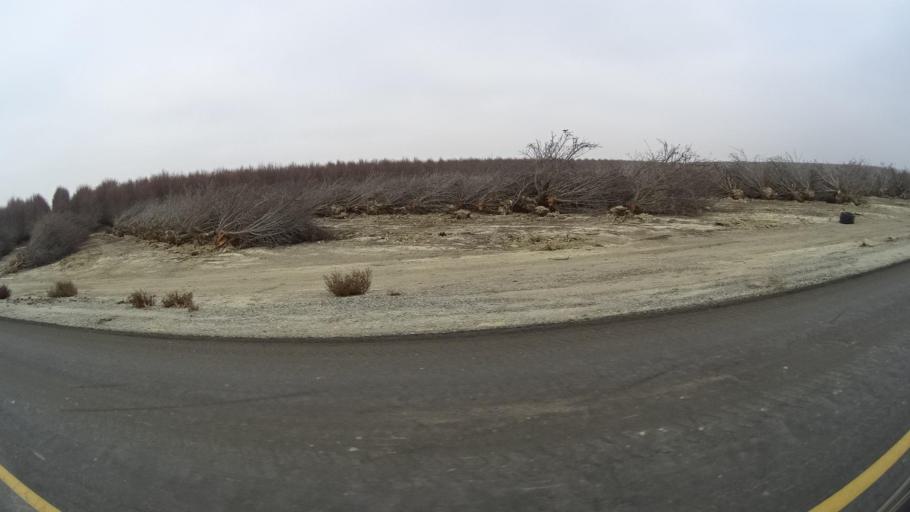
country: US
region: California
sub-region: Kern County
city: Maricopa
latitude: 35.1188
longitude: -119.3572
